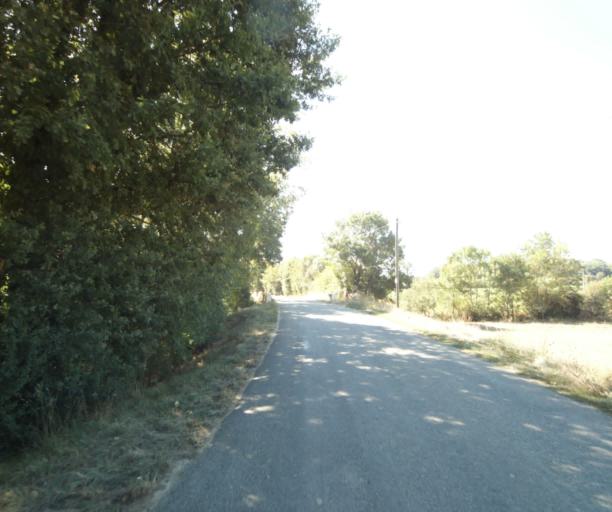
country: FR
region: Midi-Pyrenees
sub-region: Departement du Tarn-et-Garonne
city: Verdun-sur-Garonne
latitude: 43.8435
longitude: 1.2014
